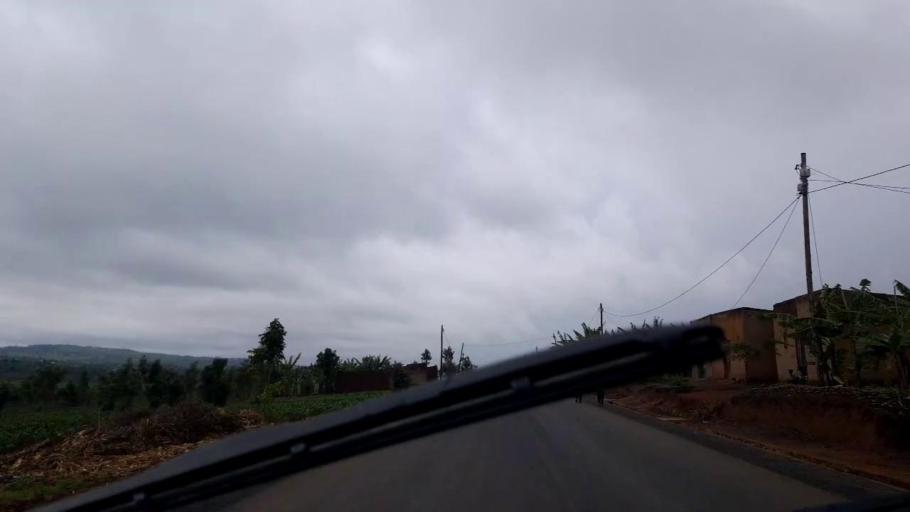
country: RW
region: Northern Province
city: Byumba
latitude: -1.4233
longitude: 30.2769
